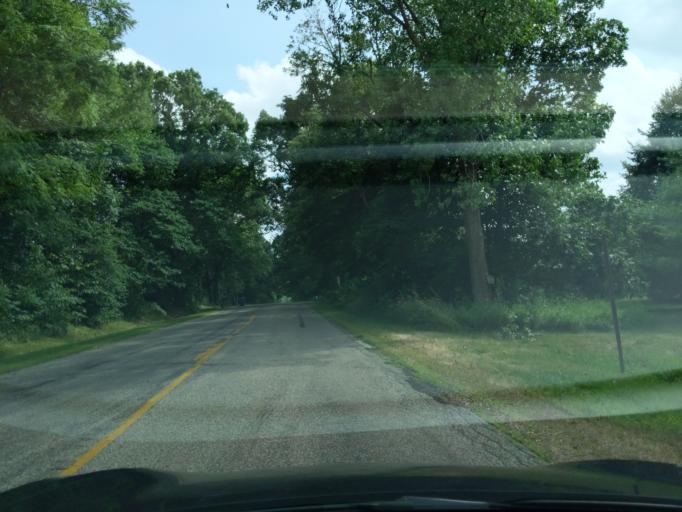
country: US
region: Michigan
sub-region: Eaton County
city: Eaton Rapids
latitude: 42.5238
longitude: -84.6016
